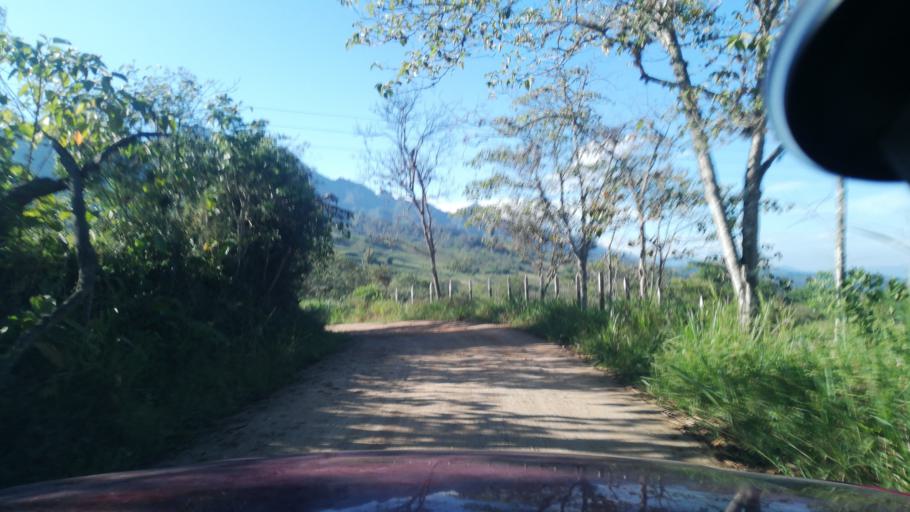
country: CO
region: Cundinamarca
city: Viani
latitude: 4.8232
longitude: -74.6162
